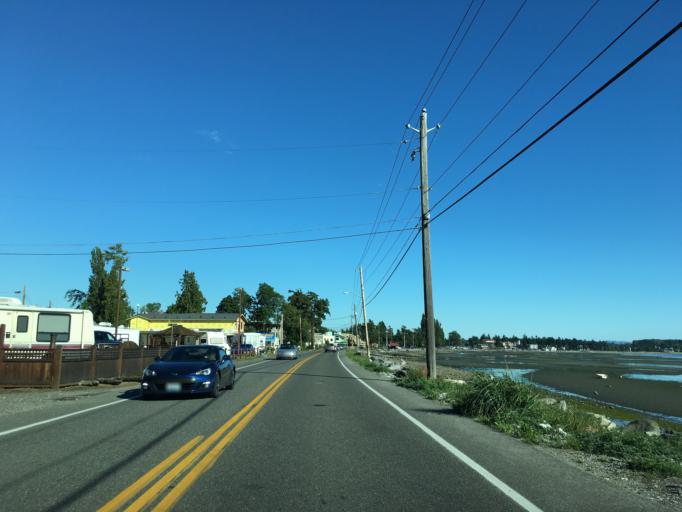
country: US
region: Washington
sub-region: Whatcom County
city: Birch Bay
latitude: 48.9361
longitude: -122.7511
